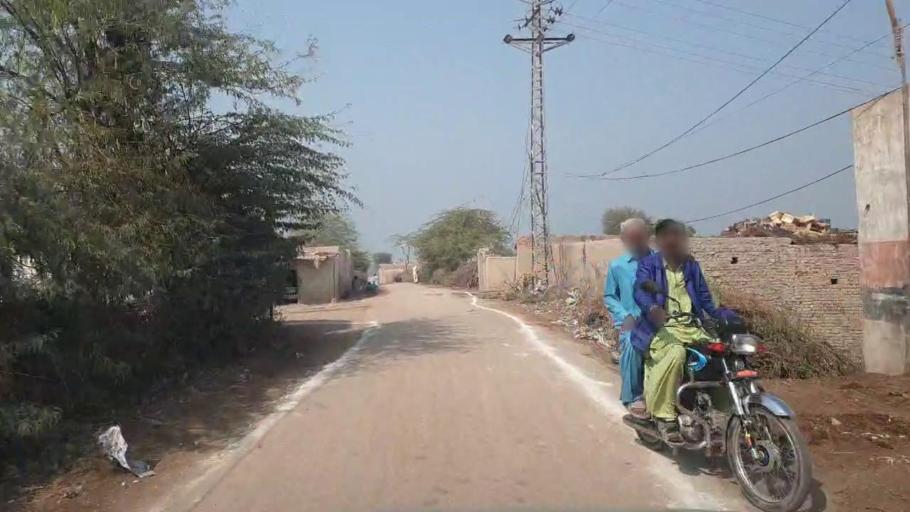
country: PK
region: Sindh
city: Hala
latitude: 25.8120
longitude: 68.4127
